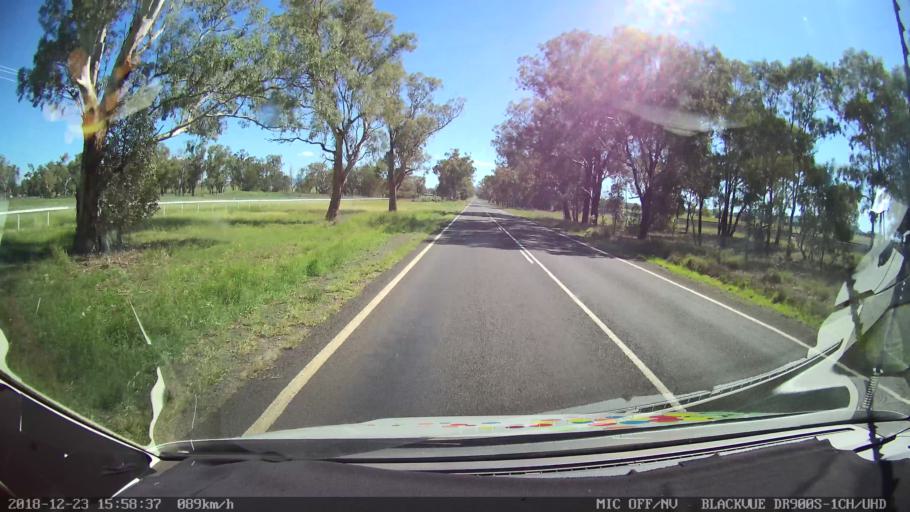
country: AU
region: New South Wales
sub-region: Tamworth Municipality
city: Phillip
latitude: -31.1904
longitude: 150.8401
